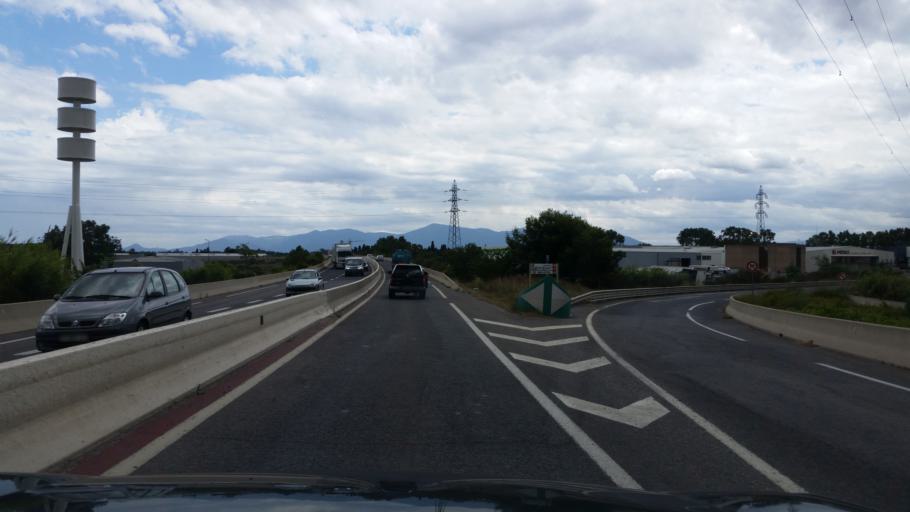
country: FR
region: Languedoc-Roussillon
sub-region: Departement des Pyrenees-Orientales
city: Toulouges
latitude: 42.6839
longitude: 2.8554
